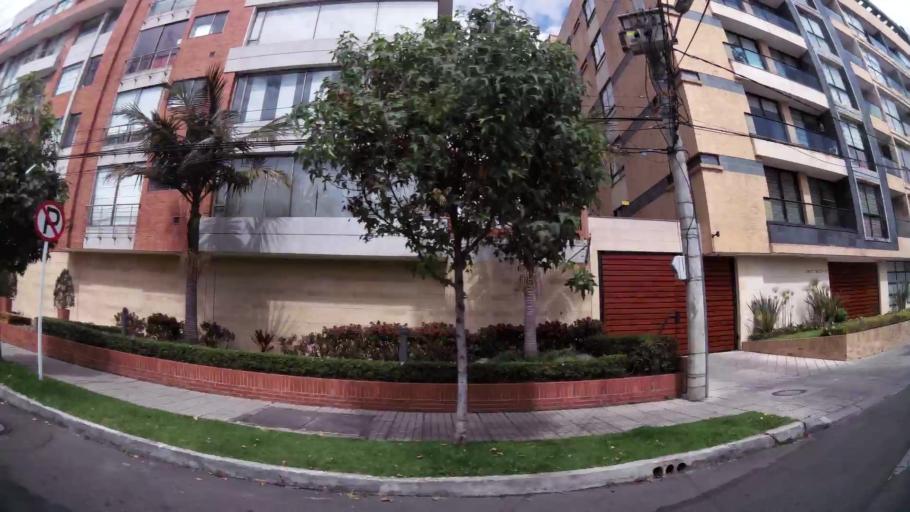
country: CO
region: Bogota D.C.
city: Barrio San Luis
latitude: 4.7028
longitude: -74.0453
